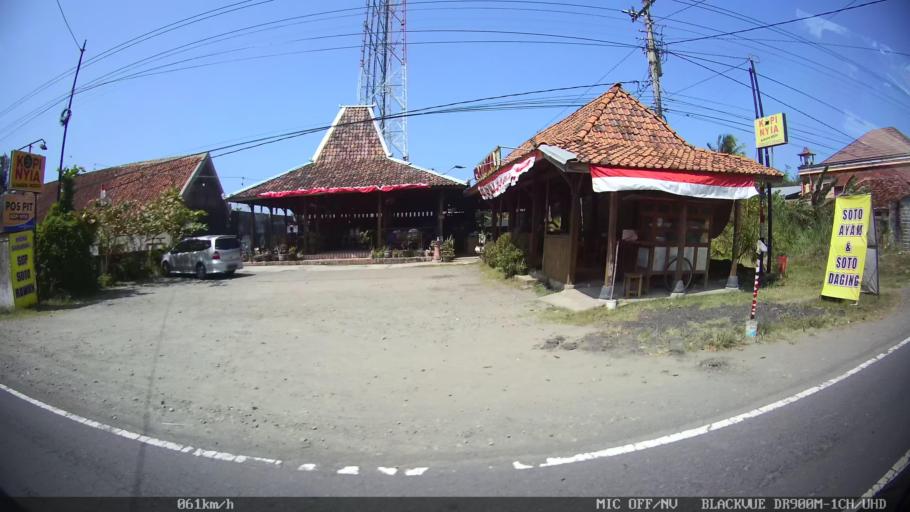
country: ID
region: Daerah Istimewa Yogyakarta
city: Srandakan
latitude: -7.8871
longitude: 110.0793
